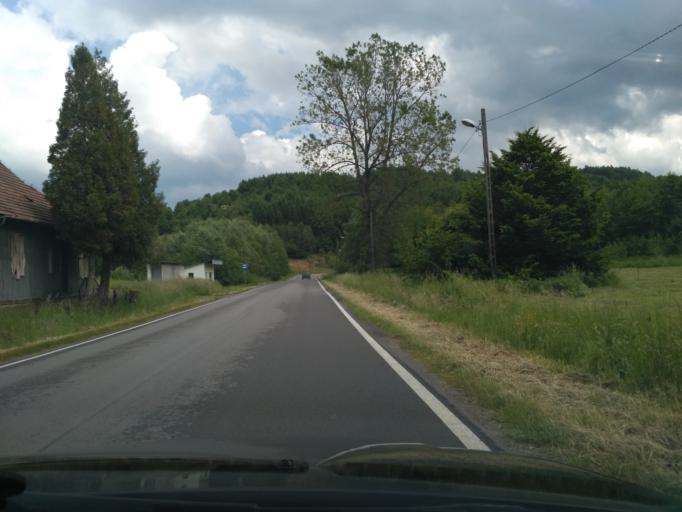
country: PL
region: Subcarpathian Voivodeship
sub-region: Powiat przeworski
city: Jawornik Polski
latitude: 49.9107
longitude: 22.3008
